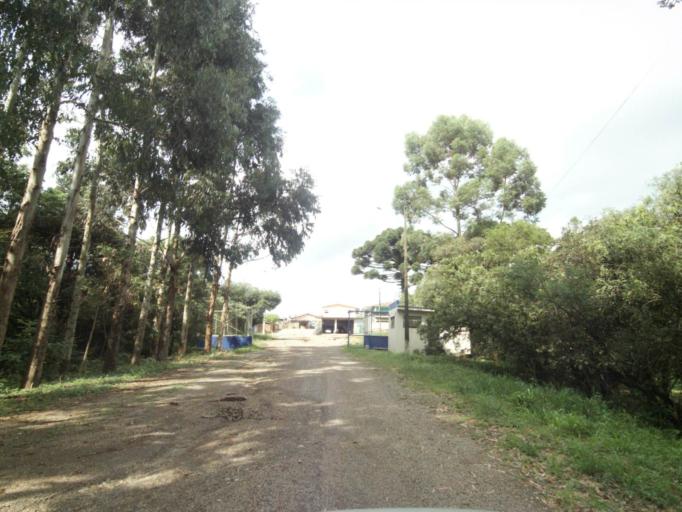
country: BR
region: Rio Grande do Sul
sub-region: Lagoa Vermelha
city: Lagoa Vermelha
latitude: -28.2221
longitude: -51.5108
